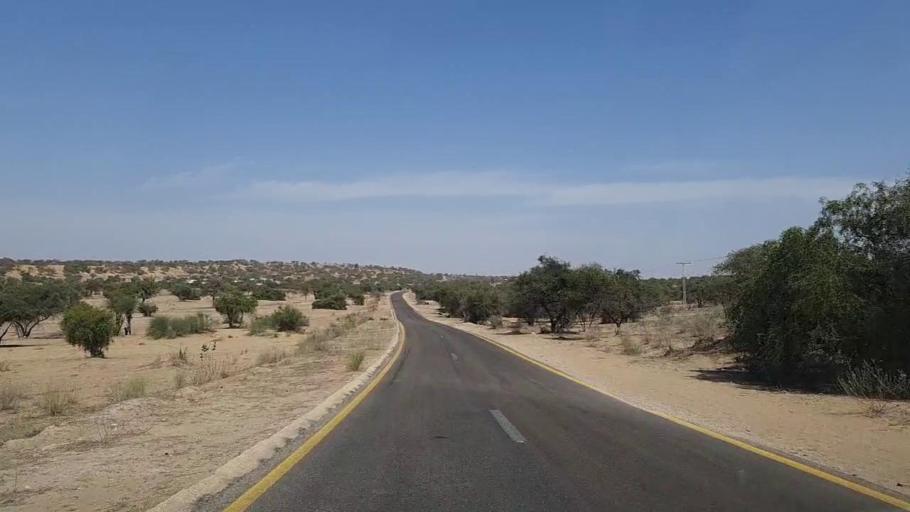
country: PK
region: Sindh
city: Mithi
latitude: 24.8871
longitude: 69.8750
